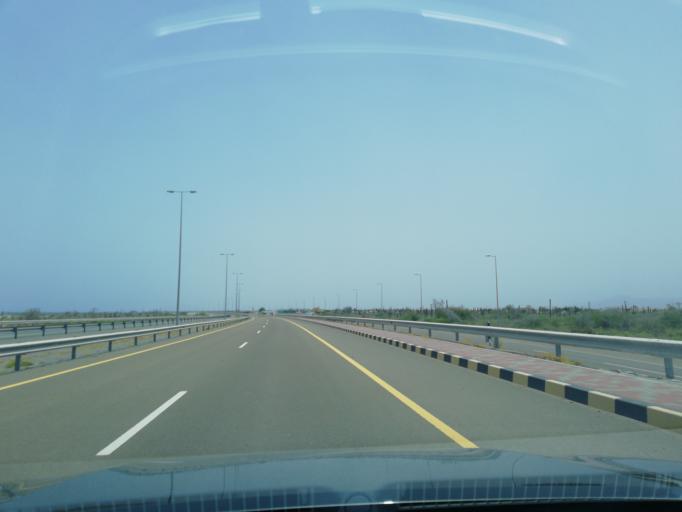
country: OM
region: Al Batinah
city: Shinas
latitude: 24.8770
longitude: 56.4051
